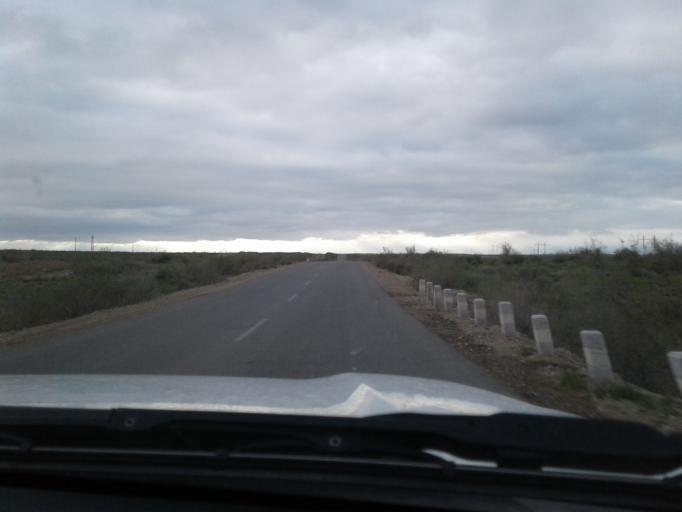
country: TM
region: Lebap
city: Sayat
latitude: 38.9139
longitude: 64.3179
